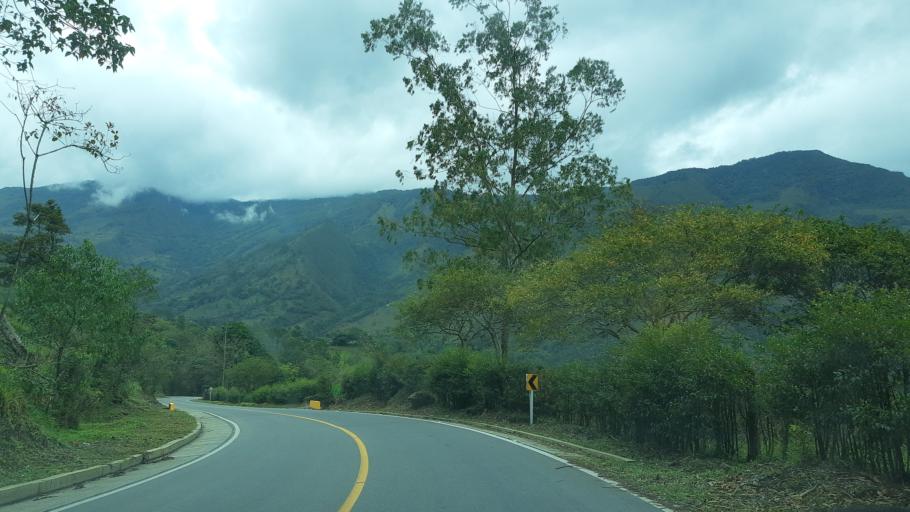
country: CO
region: Boyaca
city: Chivor
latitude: 4.9543
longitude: -73.3108
